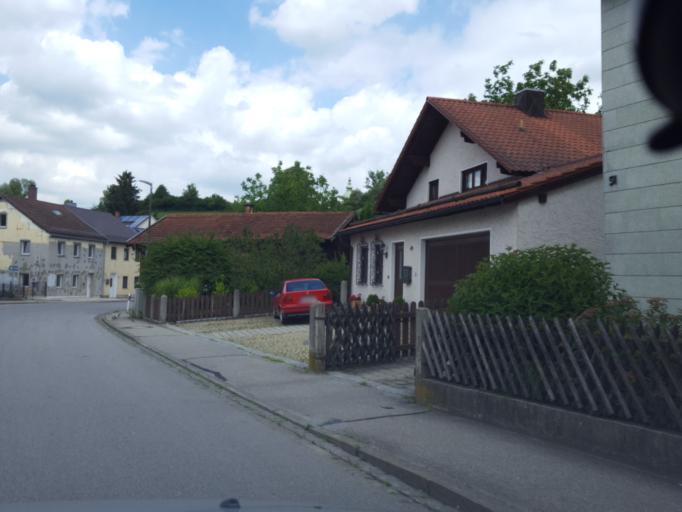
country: DE
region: Bavaria
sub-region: Upper Bavaria
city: Neumarkt-Sankt Veit
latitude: 48.3557
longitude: 12.5128
